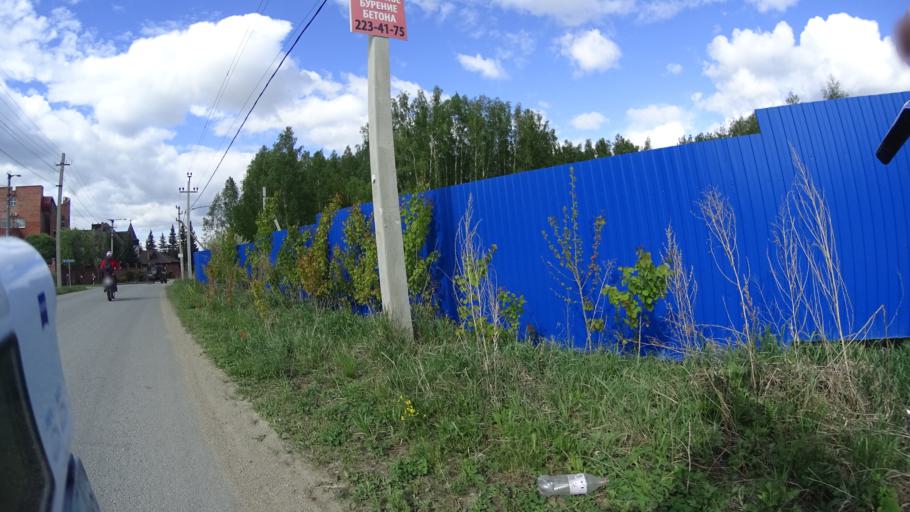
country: RU
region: Chelyabinsk
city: Sargazy
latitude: 55.1496
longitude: 61.2377
